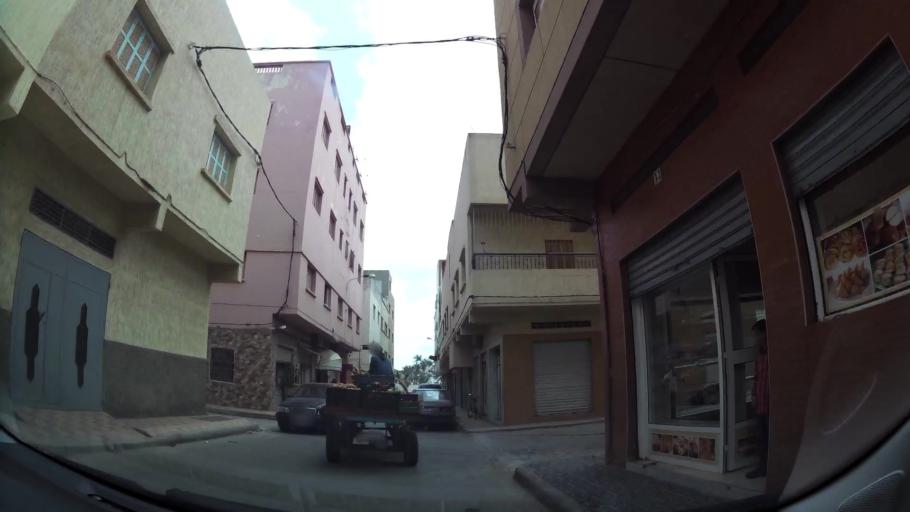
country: MA
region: Oriental
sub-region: Nador
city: Nador
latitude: 35.1714
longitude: -2.9255
